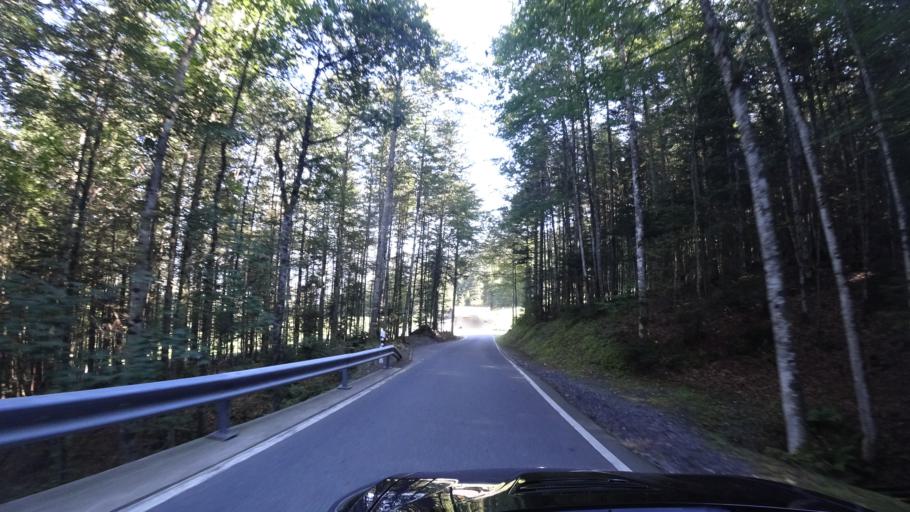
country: CH
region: Obwalden
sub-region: Obwalden
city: Giswil
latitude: 46.8303
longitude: 8.1259
